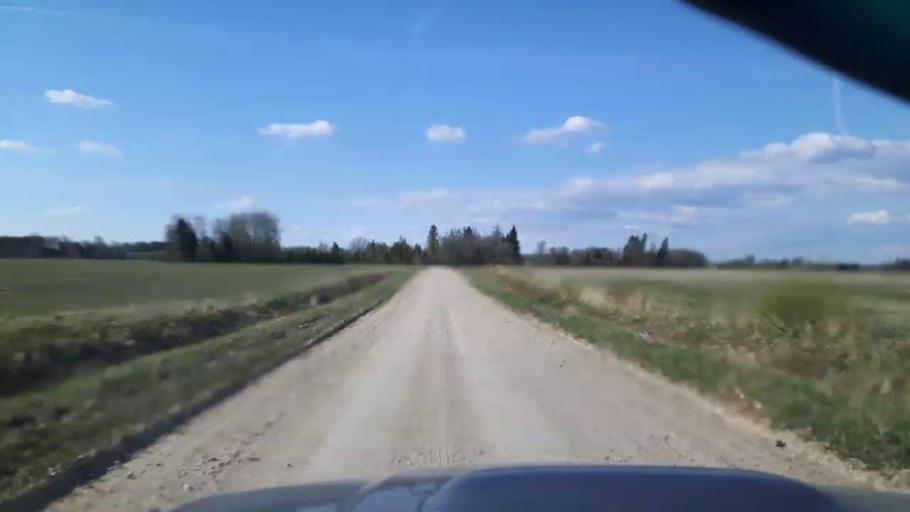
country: EE
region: Paernumaa
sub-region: Tootsi vald
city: Tootsi
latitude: 58.4406
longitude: 24.8549
